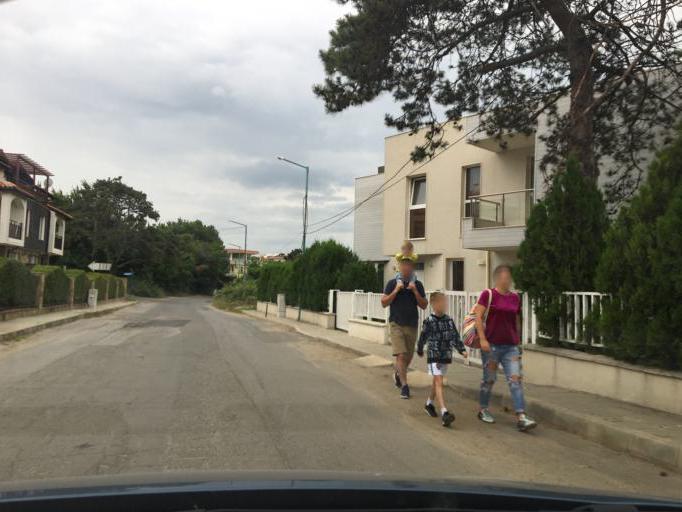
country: BG
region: Burgas
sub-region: Obshtina Sozopol
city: Sozopol
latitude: 42.4072
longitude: 27.7165
